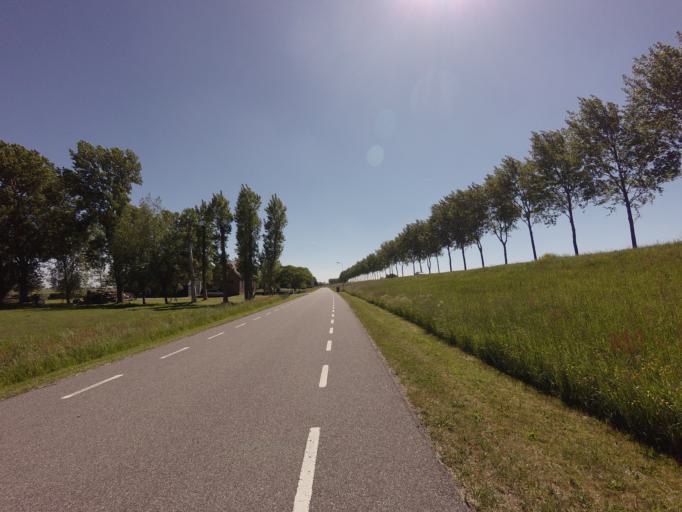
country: NL
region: North Holland
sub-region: Gemeente Alkmaar
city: Alkmaar
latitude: 52.5818
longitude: 4.7520
